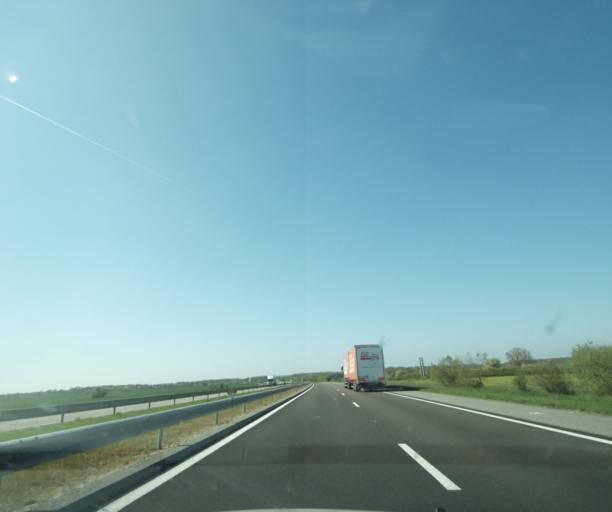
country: FR
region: Centre
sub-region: Departement du Loiret
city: Briare
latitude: 47.6319
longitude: 2.7845
